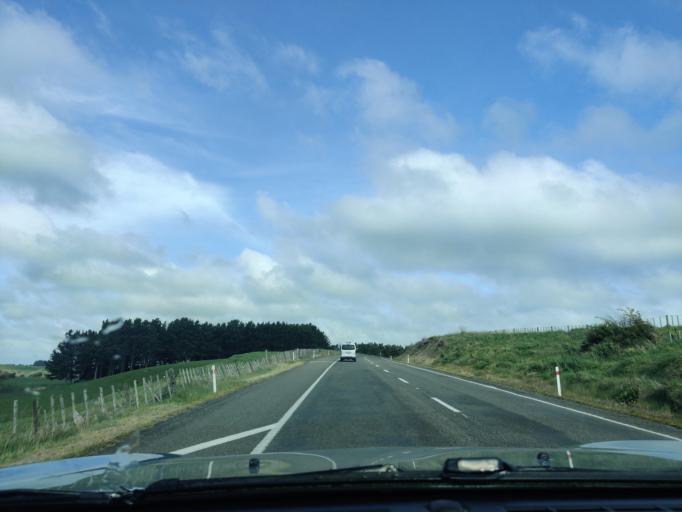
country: NZ
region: Manawatu-Wanganui
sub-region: Rangitikei District
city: Bulls
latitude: -40.0728
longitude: 175.2323
